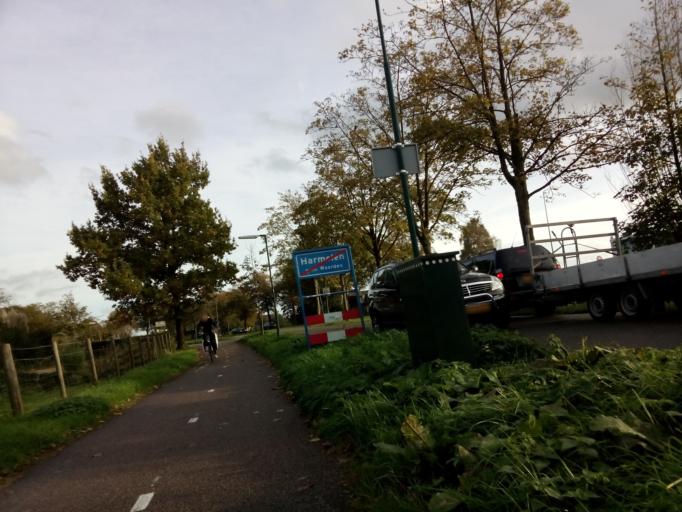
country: NL
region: Utrecht
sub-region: Gemeente Montfoort
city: Montfoort
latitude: 52.0892
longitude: 4.9720
